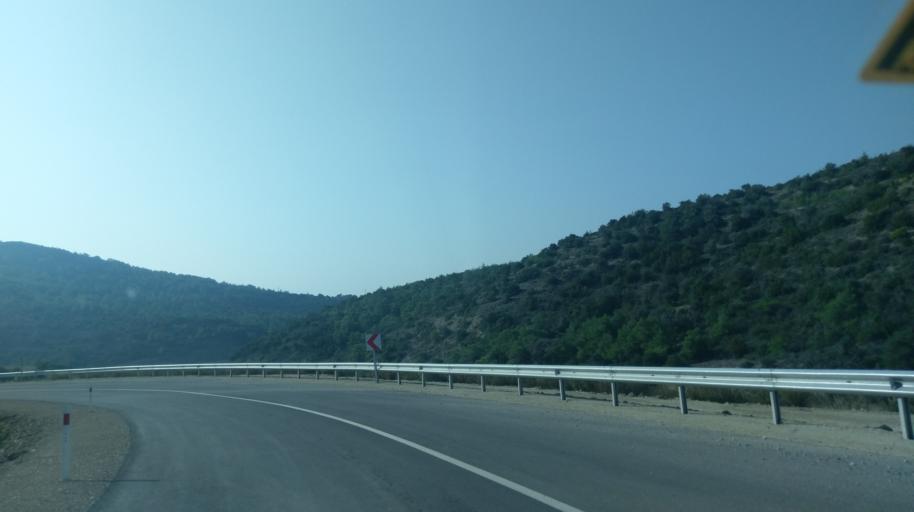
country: CY
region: Ammochostos
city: Leonarisso
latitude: 35.5354
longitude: 34.2509
